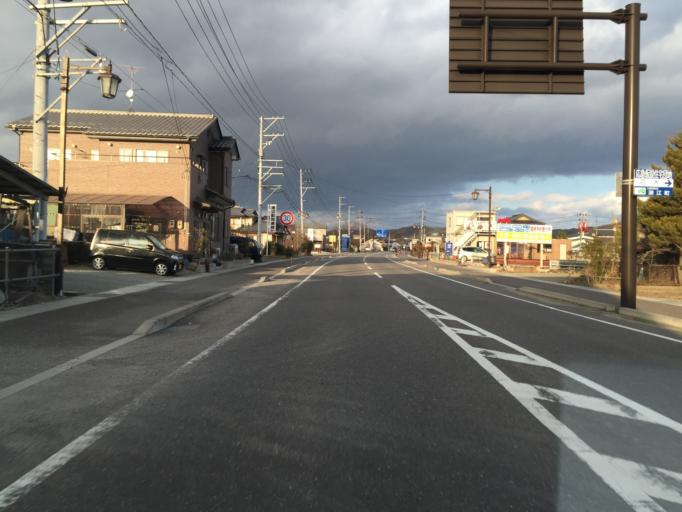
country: JP
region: Fukushima
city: Motomiya
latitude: 37.5141
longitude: 140.4066
